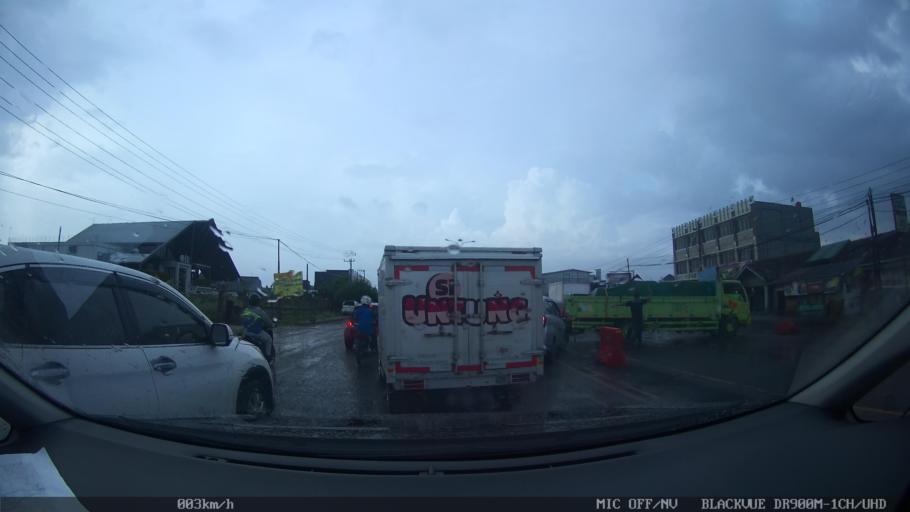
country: ID
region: Lampung
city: Kedaton
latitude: -5.3945
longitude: 105.2891
